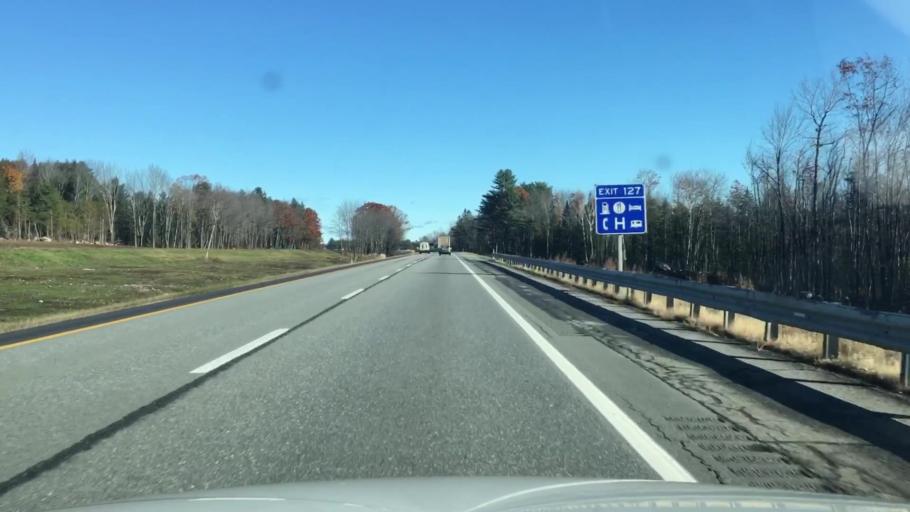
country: US
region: Maine
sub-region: Kennebec County
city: Oakland
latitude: 44.5376
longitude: -69.6849
